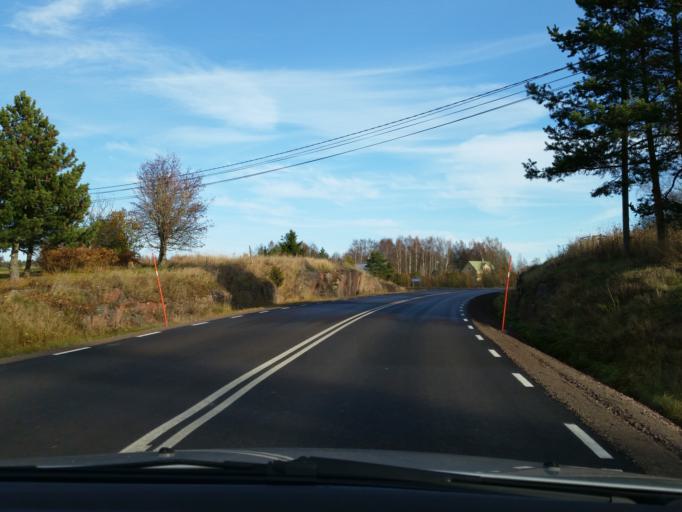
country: AX
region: Alands landsbygd
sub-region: Finstroem
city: Finstroem
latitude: 60.3155
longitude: 19.9818
